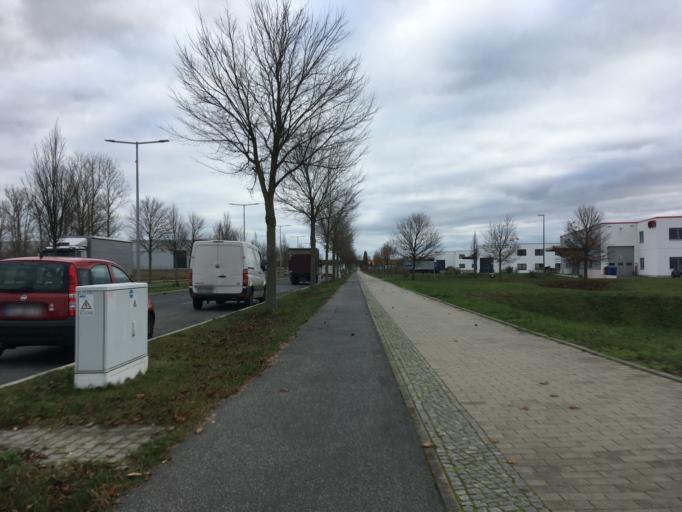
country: DE
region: Berlin
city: Altglienicke
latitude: 52.3944
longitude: 13.5431
